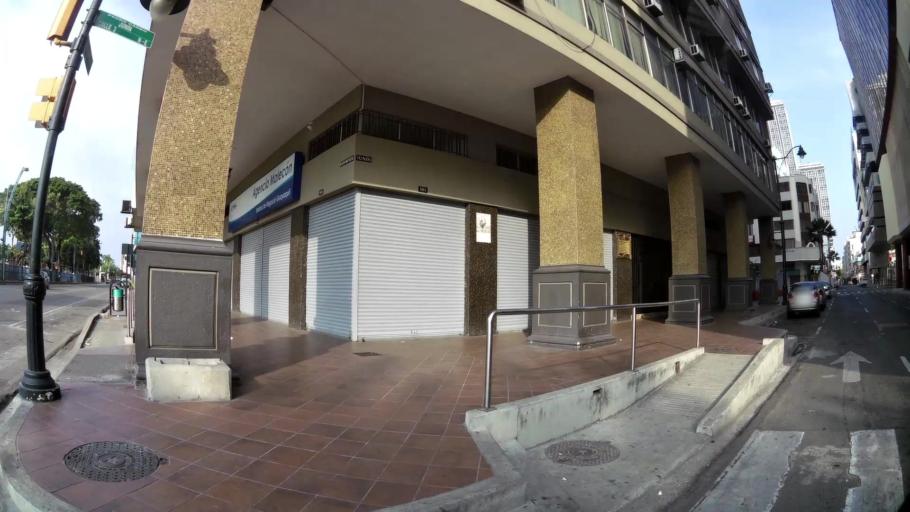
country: EC
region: Guayas
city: Eloy Alfaro
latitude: -2.1905
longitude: -79.8792
